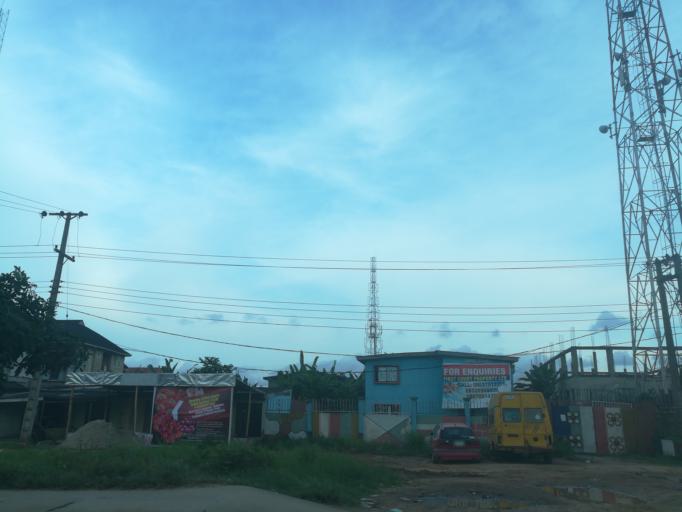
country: NG
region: Lagos
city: Ebute Ikorodu
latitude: 6.6229
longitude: 3.4823
